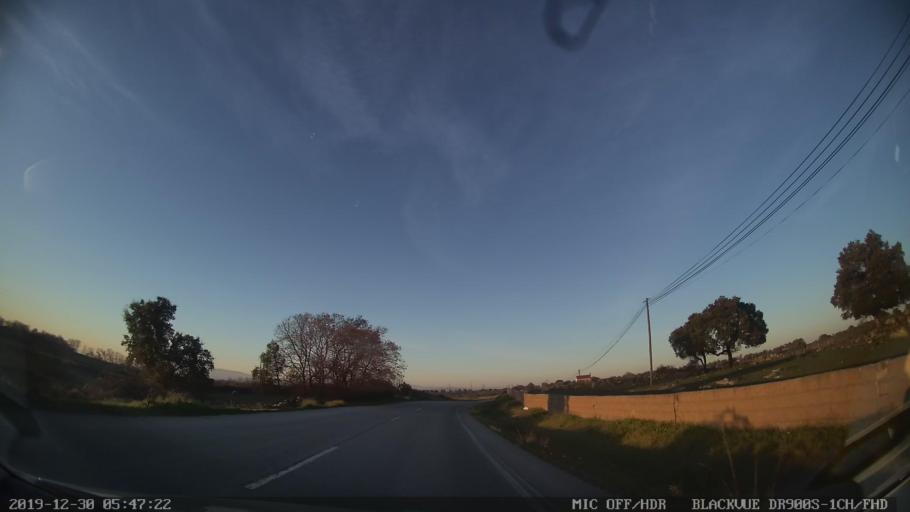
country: PT
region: Castelo Branco
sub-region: Idanha-A-Nova
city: Idanha-a-Nova
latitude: 39.9499
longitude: -7.2394
